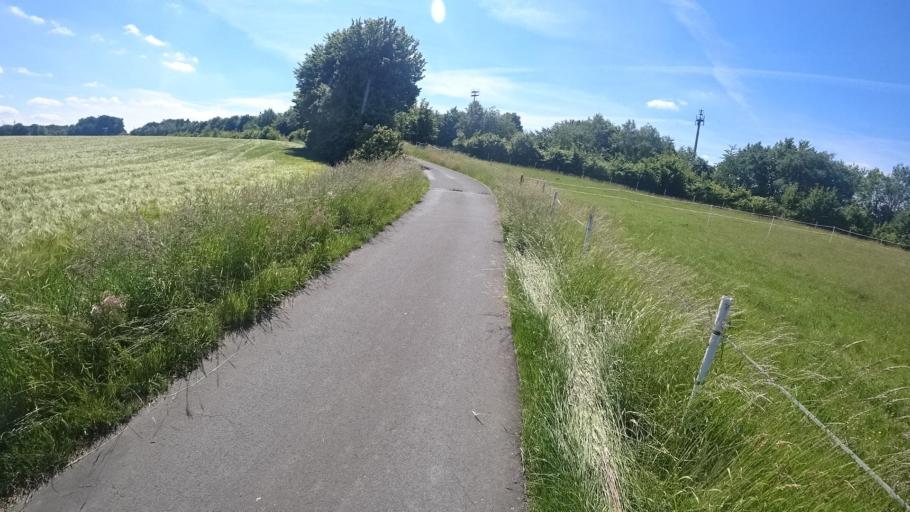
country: DE
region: Rheinland-Pfalz
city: Mammelzen
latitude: 50.6958
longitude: 7.6589
